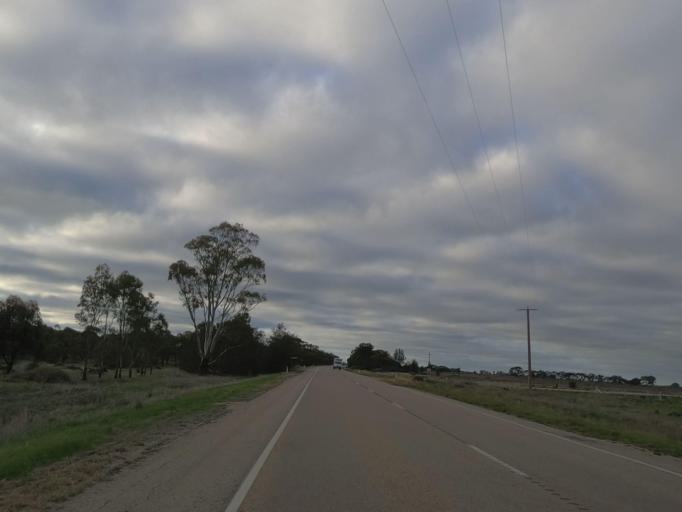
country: AU
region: Victoria
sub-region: Swan Hill
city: Swan Hill
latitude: -35.8224
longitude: 143.9493
